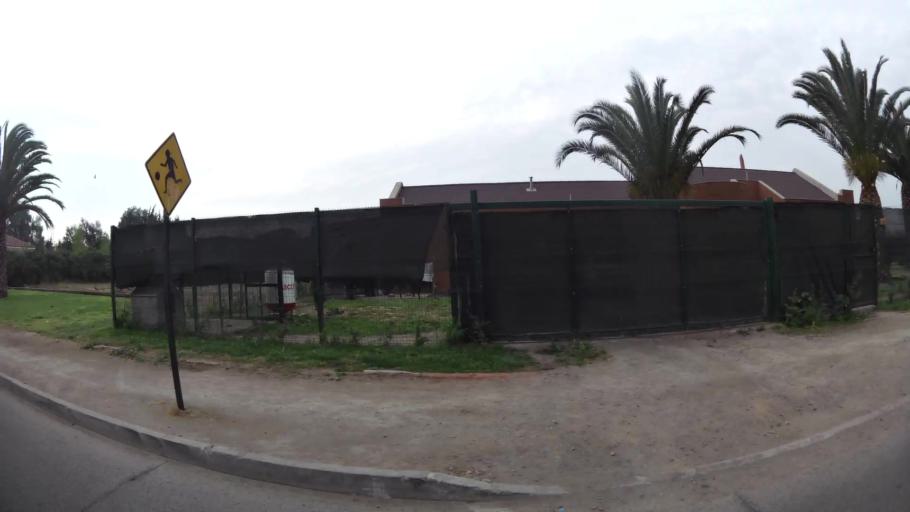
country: CL
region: Santiago Metropolitan
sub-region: Provincia de Chacabuco
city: Chicureo Abajo
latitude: -33.2765
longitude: -70.7036
